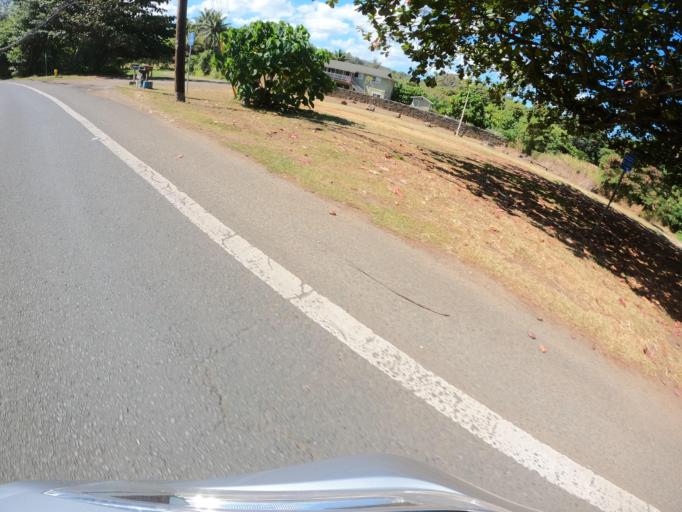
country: US
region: Hawaii
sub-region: Honolulu County
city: La'ie
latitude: 21.6334
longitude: -157.9212
